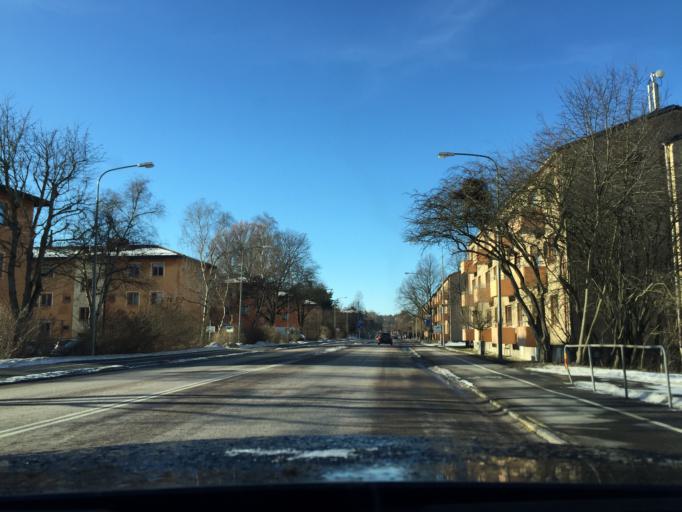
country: SE
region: Stockholm
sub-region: Stockholms Kommun
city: Bromma
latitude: 59.3420
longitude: 17.9498
